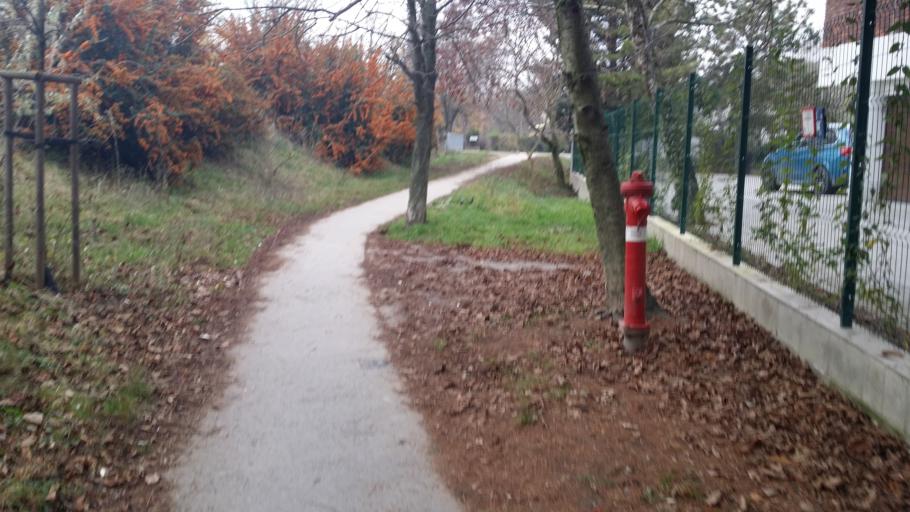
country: HU
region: Pest
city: Budakalasz
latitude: 47.5935
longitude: 19.0580
